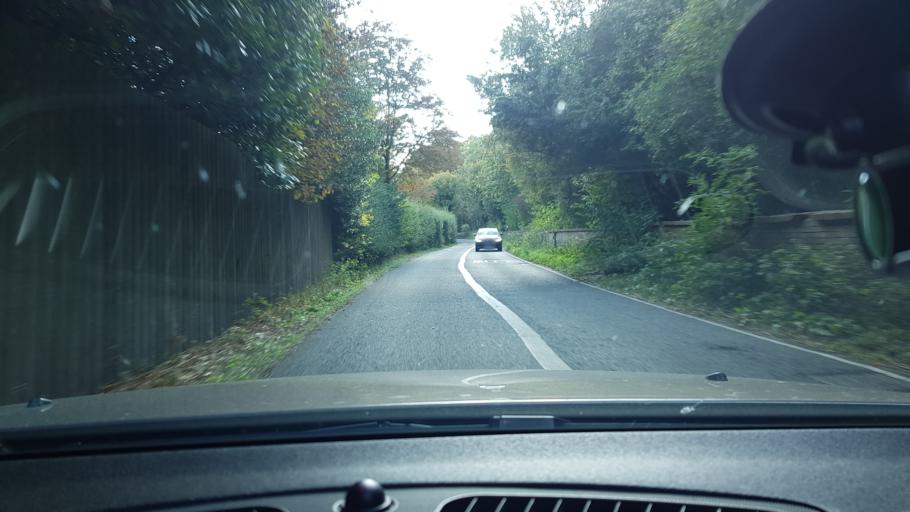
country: GB
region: England
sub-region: West Berkshire
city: Kintbury
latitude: 51.4071
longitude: -1.4448
